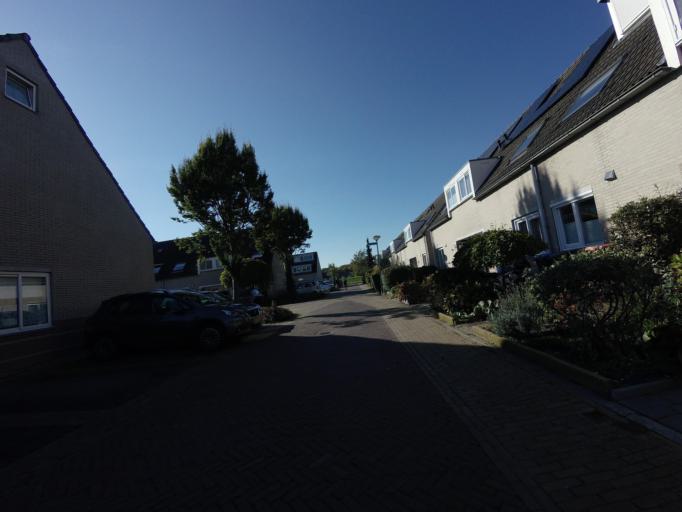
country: NL
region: North Holland
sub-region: Gemeente Naarden
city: Naarden
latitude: 52.3245
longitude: 5.1216
